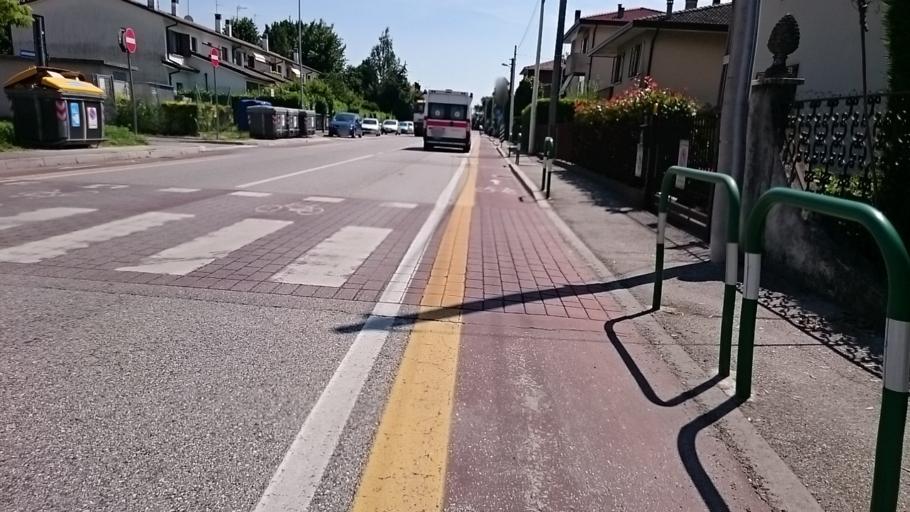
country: IT
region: Veneto
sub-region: Provincia di Padova
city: Padova
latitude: 45.4028
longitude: 11.9114
